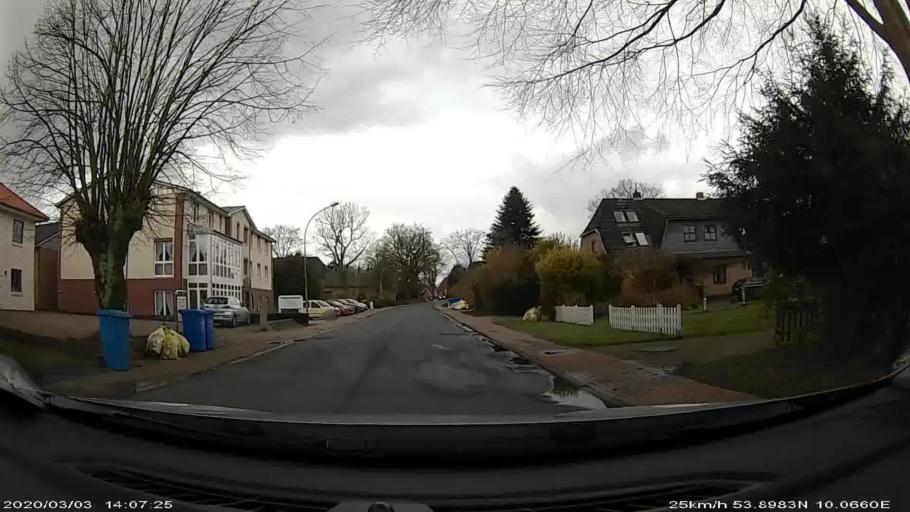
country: DE
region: Schleswig-Holstein
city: Hartenholm
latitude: 53.8986
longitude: 10.0656
